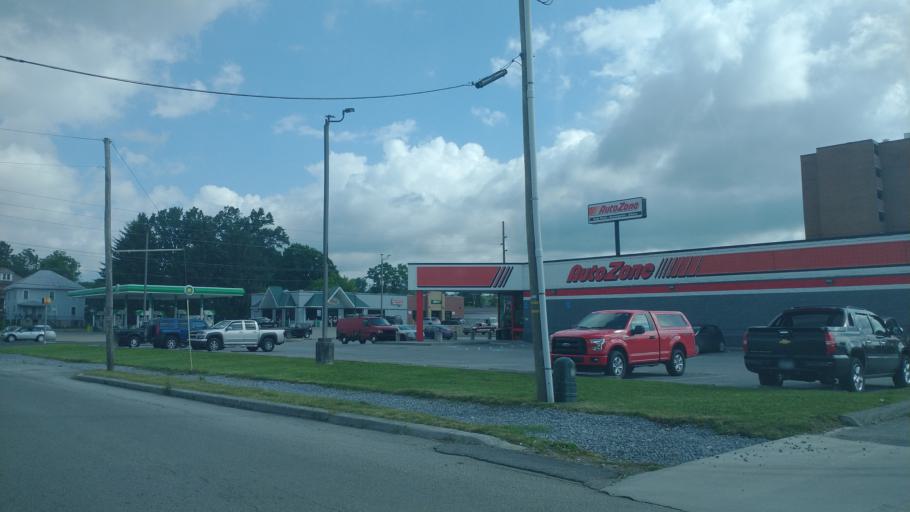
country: US
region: West Virginia
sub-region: Mercer County
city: Princeton
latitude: 37.3638
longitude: -81.0926
